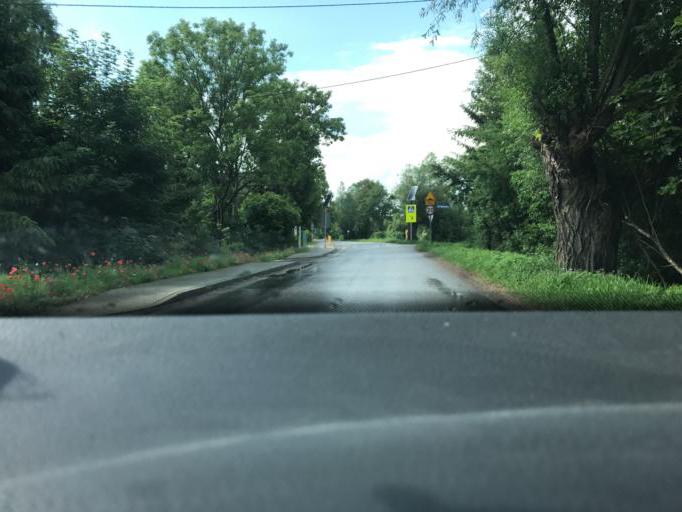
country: PL
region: Pomeranian Voivodeship
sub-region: Powiat gdanski
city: Cedry Wielkie
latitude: 54.3309
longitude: 18.8008
